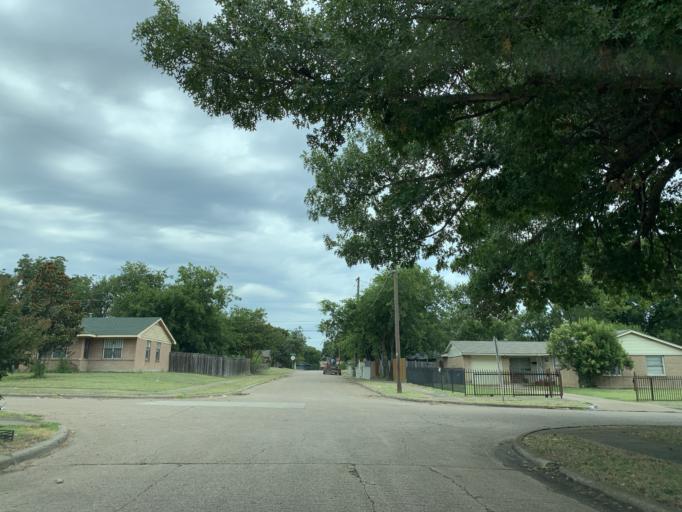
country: US
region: Texas
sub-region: Dallas County
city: DeSoto
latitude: 32.6587
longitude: -96.8269
